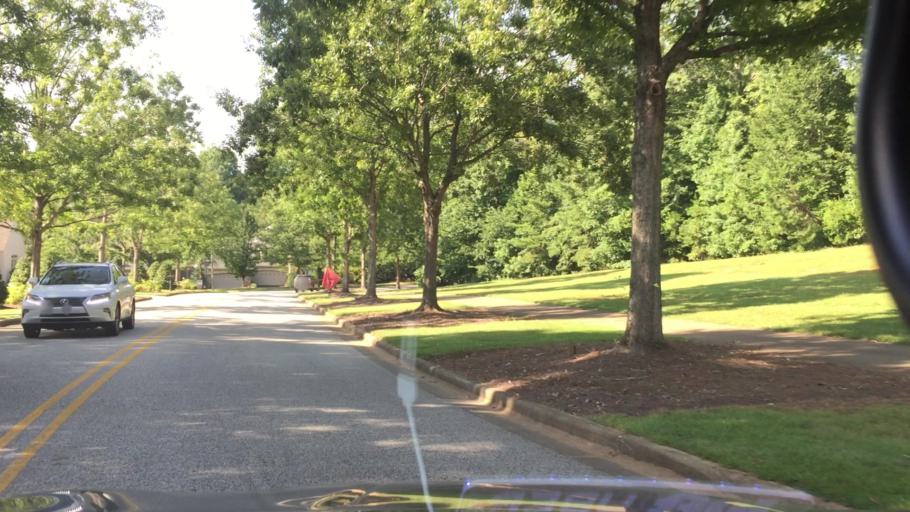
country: US
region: Alabama
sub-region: Lee County
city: Auburn
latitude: 32.5812
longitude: -85.4439
